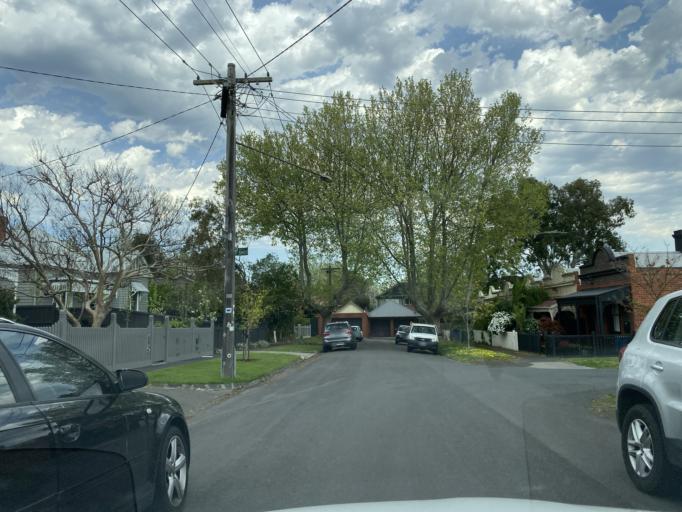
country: AU
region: Victoria
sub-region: Boroondara
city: Canterbury
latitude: -37.8289
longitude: 145.0839
